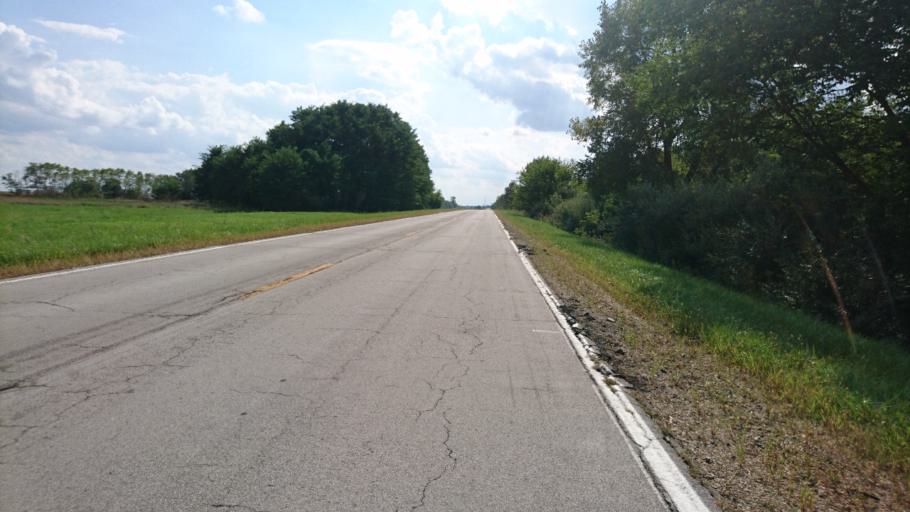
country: US
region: Illinois
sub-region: Logan County
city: Atlanta
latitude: 40.3462
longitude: -89.1323
